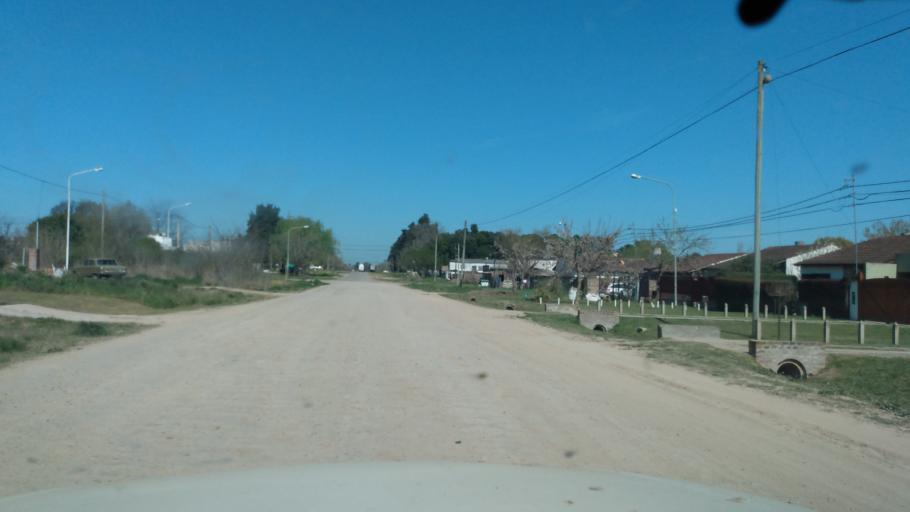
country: AR
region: Buenos Aires
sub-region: Partido de Lujan
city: Lujan
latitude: -34.5677
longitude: -59.1392
